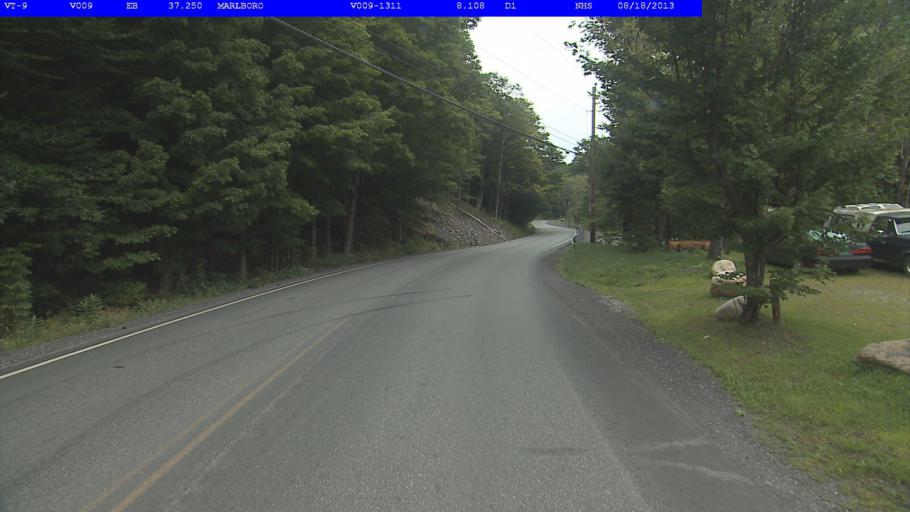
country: US
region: Vermont
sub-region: Windham County
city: West Brattleboro
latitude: 42.8777
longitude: -72.6819
